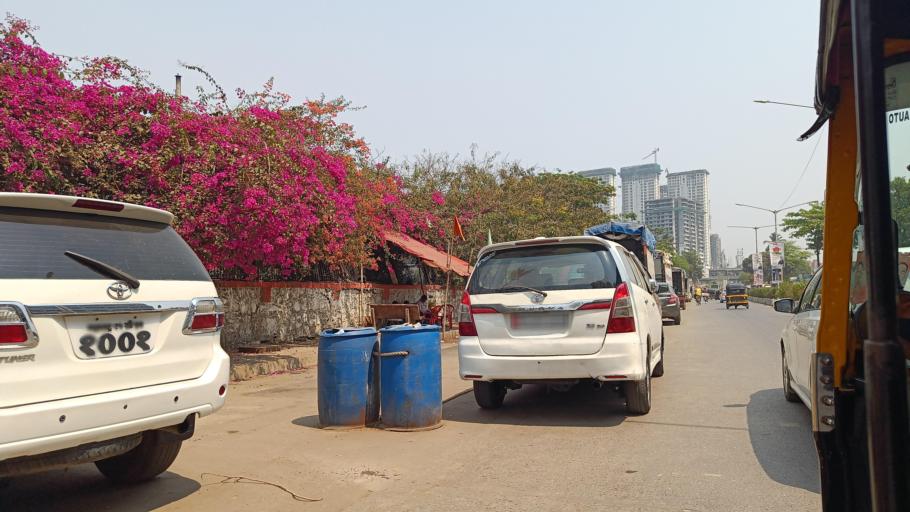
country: IN
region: Maharashtra
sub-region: Mumbai Suburban
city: Powai
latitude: 19.1493
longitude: 72.8402
